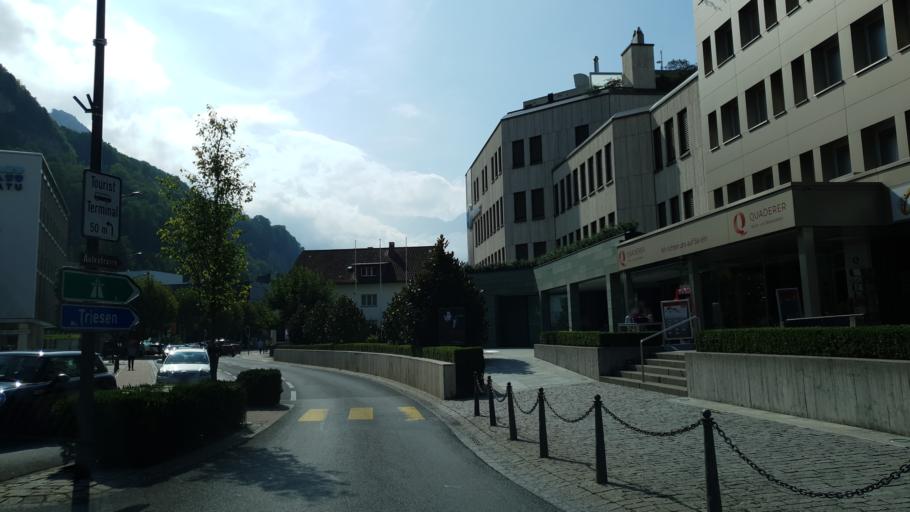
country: LI
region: Vaduz
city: Vaduz
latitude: 47.1410
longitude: 9.5208
